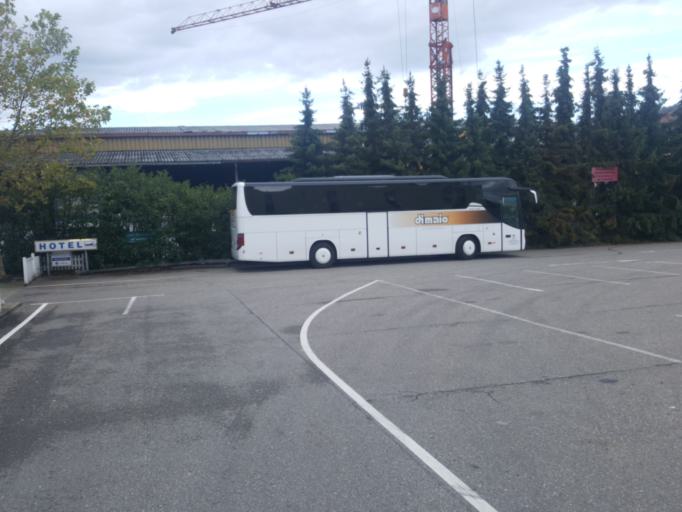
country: CH
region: Aargau
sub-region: Bezirk Rheinfelden
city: Kaiseraugst
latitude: 47.5473
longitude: 7.7378
